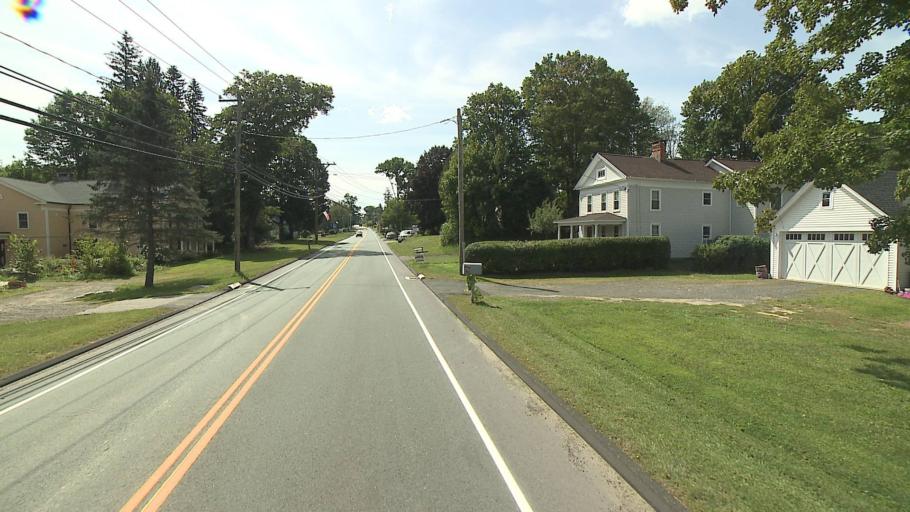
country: US
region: Connecticut
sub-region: Litchfield County
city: Bethlehem Village
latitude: 41.6368
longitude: -73.2088
